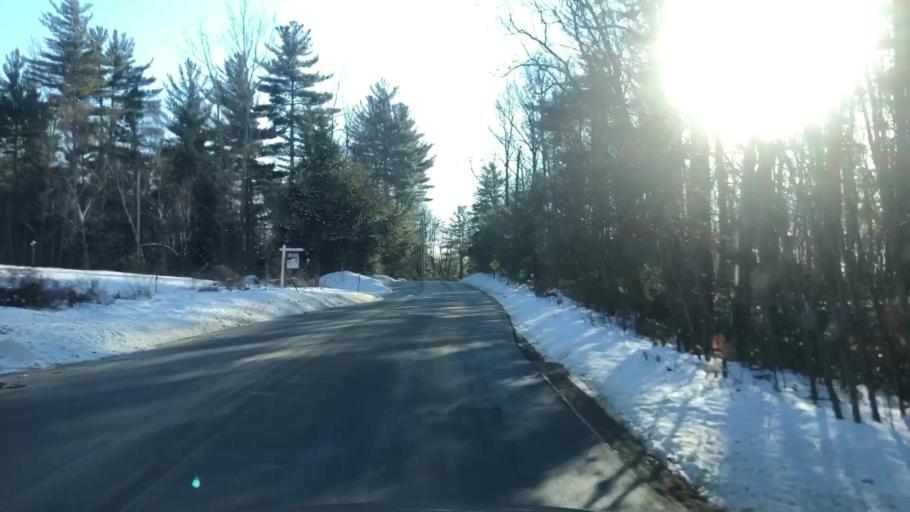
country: US
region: New Hampshire
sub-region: Hillsborough County
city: Milford
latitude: 42.8038
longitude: -71.6692
